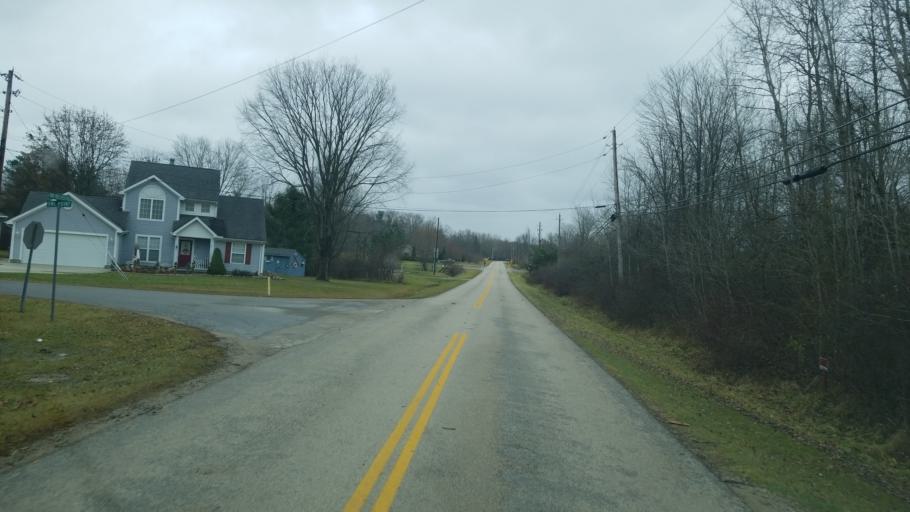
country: US
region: Ohio
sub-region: Ashtabula County
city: Roaming Shores
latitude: 41.6492
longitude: -80.8395
